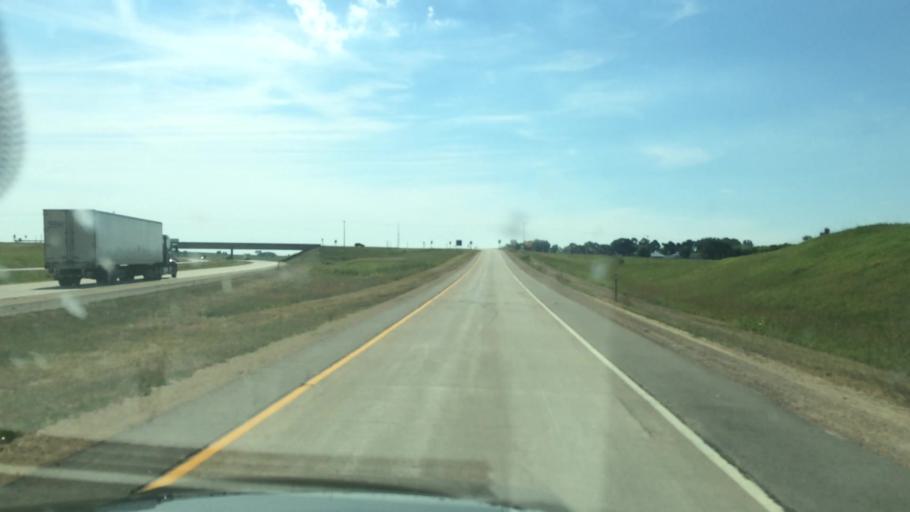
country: US
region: Wisconsin
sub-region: Shawano County
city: Bonduel
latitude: 44.7280
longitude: -88.4502
